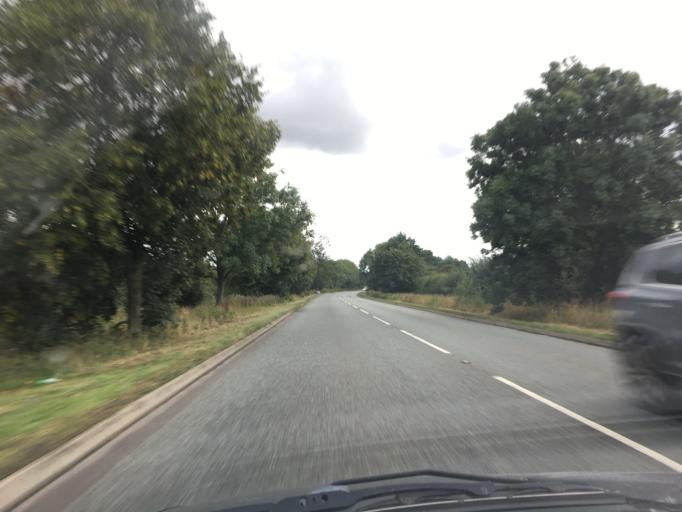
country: GB
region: England
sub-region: Leicestershire
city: Lutterworth
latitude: 52.4322
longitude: -1.2139
